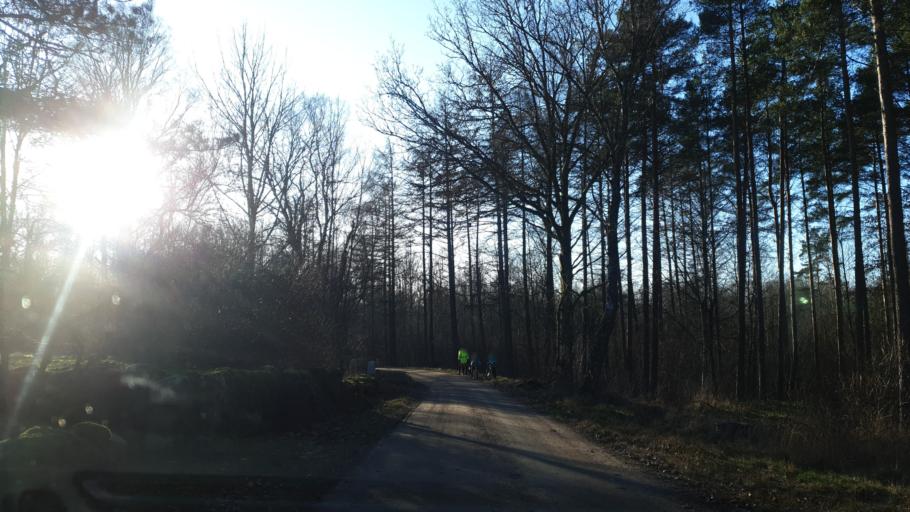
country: SE
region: Blekinge
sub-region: Karlskrona Kommun
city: Nattraby
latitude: 56.2556
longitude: 15.4090
